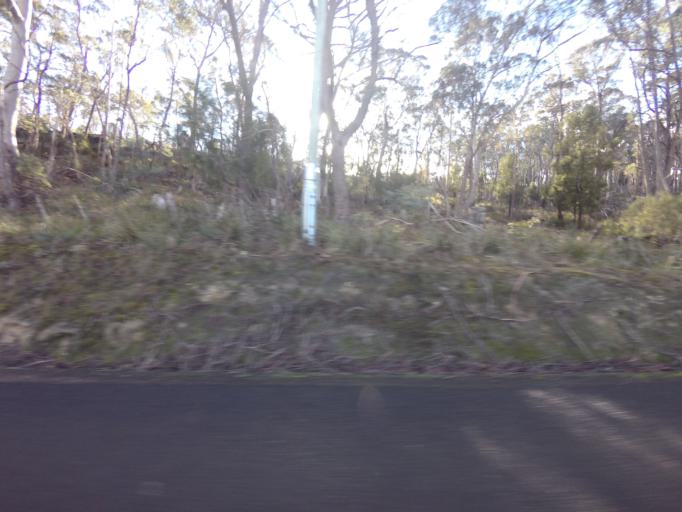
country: AU
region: Tasmania
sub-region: Glenorchy
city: Granton
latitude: -42.8038
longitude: 147.1607
